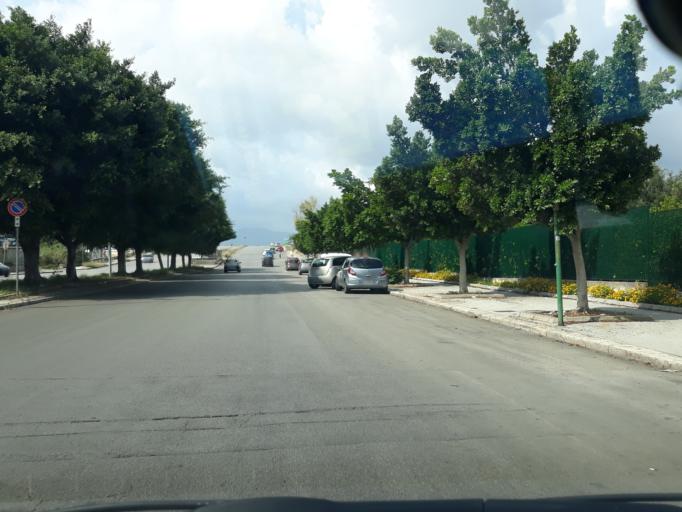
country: IT
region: Sicily
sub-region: Palermo
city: Palermo
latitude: 38.0956
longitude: 13.3423
